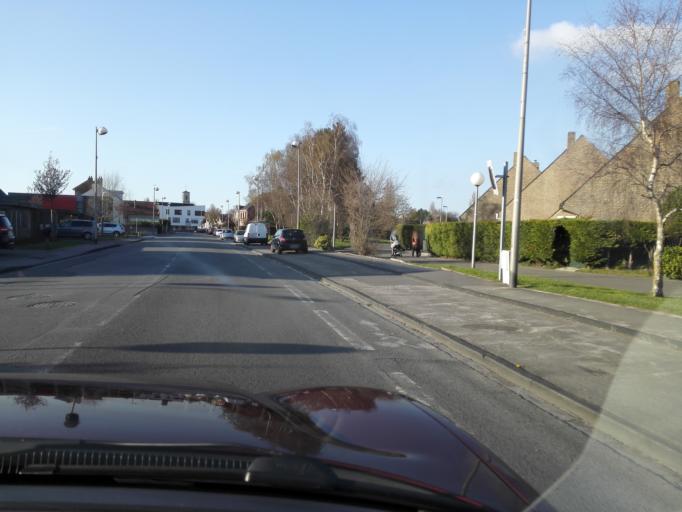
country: FR
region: Nord-Pas-de-Calais
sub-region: Departement du Nord
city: Grande-Synthe
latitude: 51.0096
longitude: 2.2954
